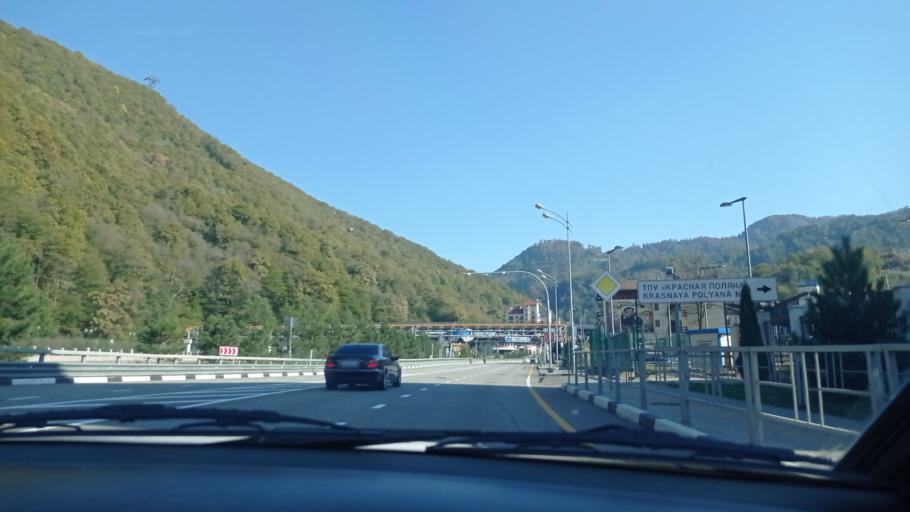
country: RU
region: Krasnodarskiy
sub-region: Sochi City
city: Krasnaya Polyana
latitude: 43.6782
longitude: 40.2807
